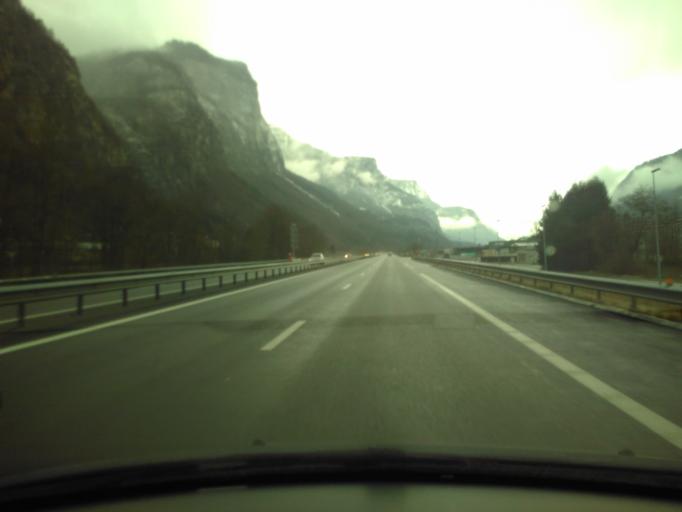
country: FR
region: Rhone-Alpes
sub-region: Departement de la Haute-Savoie
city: Magland
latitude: 46.0181
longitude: 6.6200
